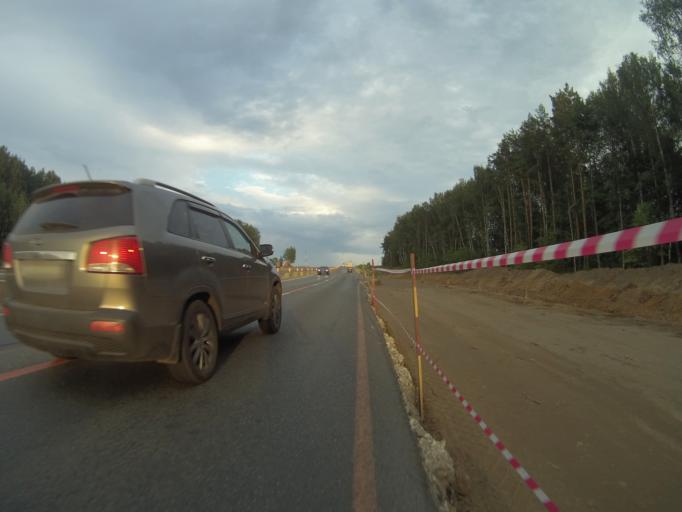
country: RU
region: Vladimir
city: Kommunar
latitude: 56.0743
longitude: 40.4844
